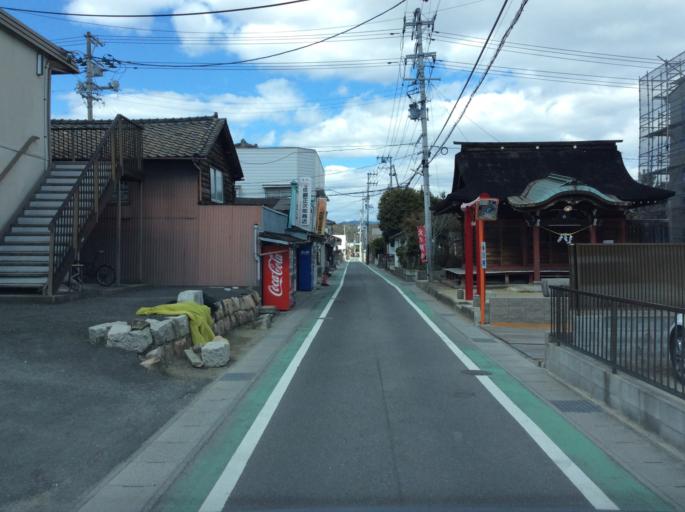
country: JP
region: Fukushima
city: Iwaki
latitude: 37.0600
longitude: 140.8960
